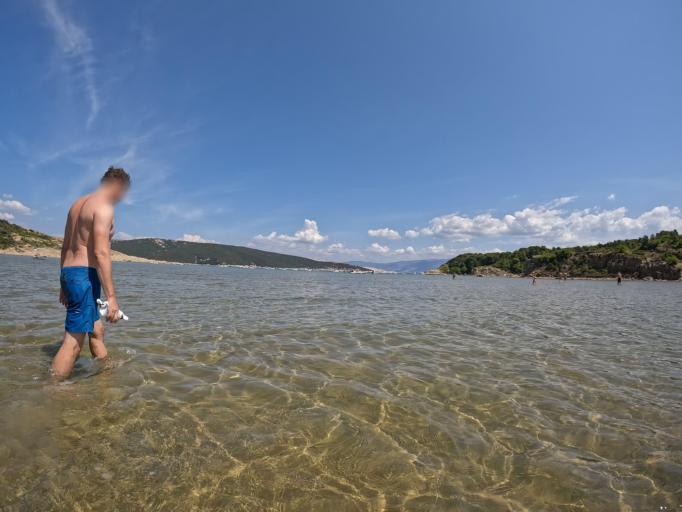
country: HR
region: Primorsko-Goranska
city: Lopar
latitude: 44.8398
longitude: 14.7518
